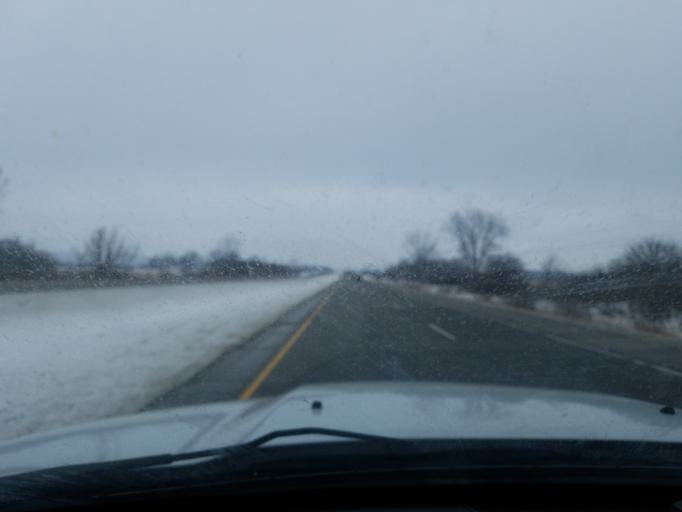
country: US
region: Indiana
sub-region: Marshall County
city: Argos
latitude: 41.2263
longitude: -86.2610
